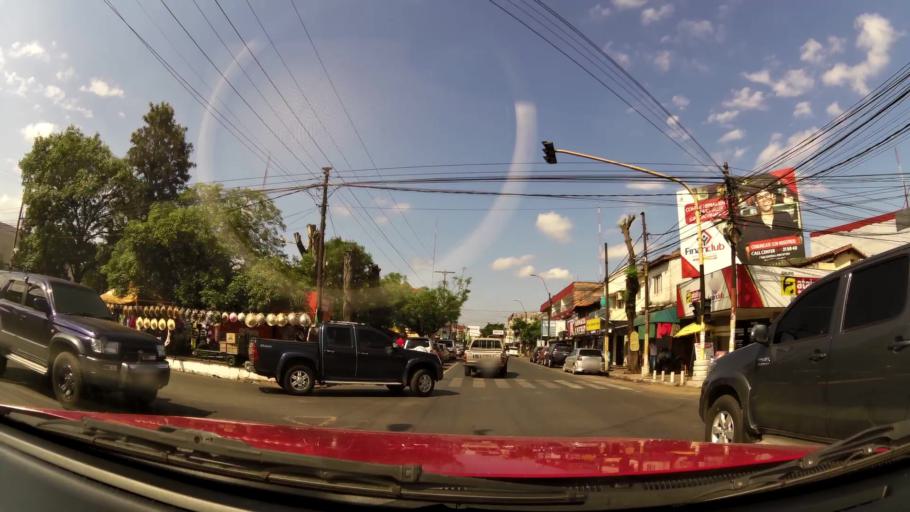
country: PY
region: Central
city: San Lorenzo
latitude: -25.3445
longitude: -57.5065
